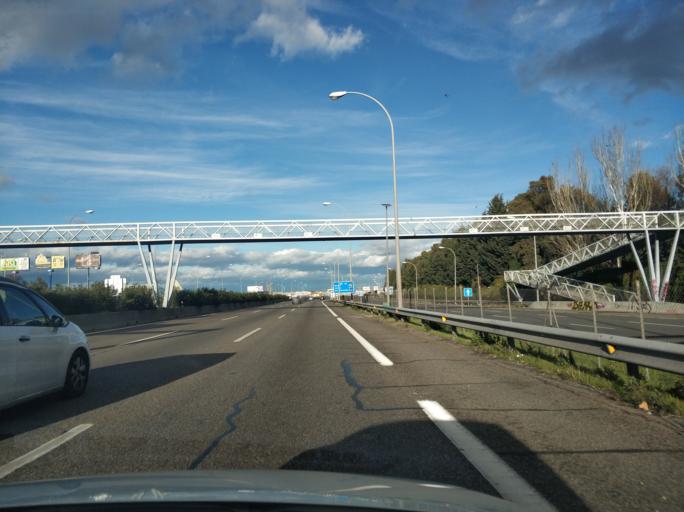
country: ES
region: Madrid
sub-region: Provincia de Madrid
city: Las Tablas
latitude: 40.5216
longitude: -3.6514
